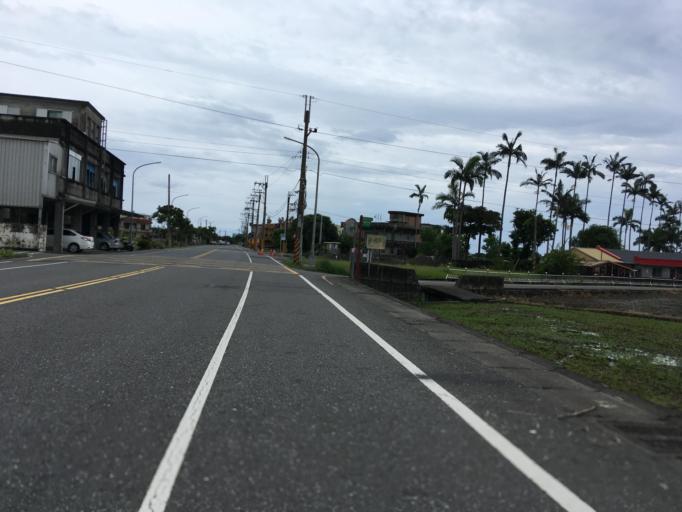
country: TW
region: Taiwan
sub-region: Yilan
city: Yilan
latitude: 24.6876
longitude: 121.8029
